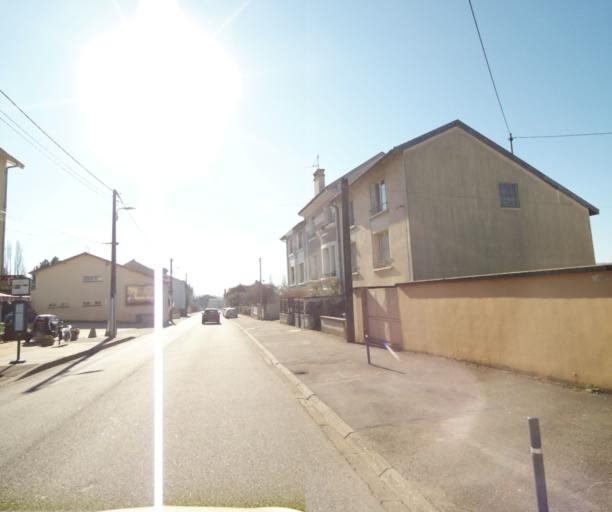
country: FR
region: Lorraine
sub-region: Departement de Meurthe-et-Moselle
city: Malzeville
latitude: 48.7221
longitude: 6.1810
